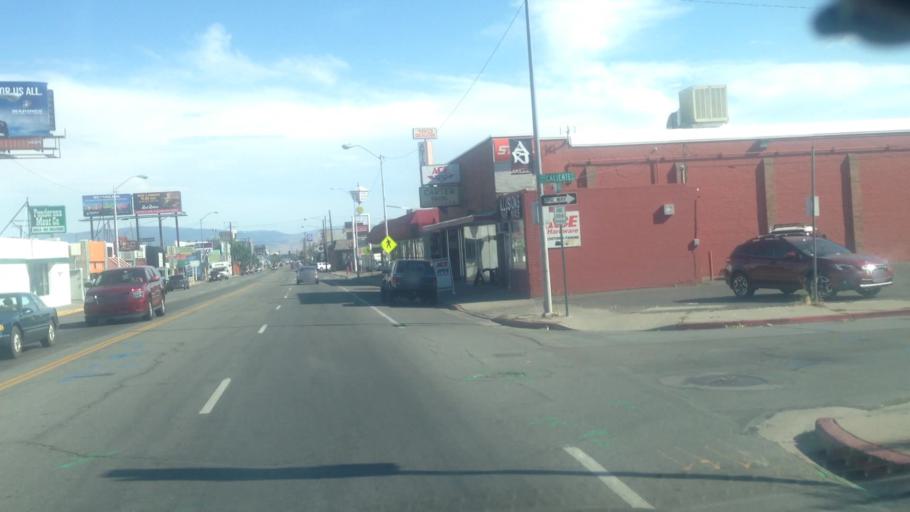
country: US
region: Nevada
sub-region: Washoe County
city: Reno
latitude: 39.5127
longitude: -119.8067
